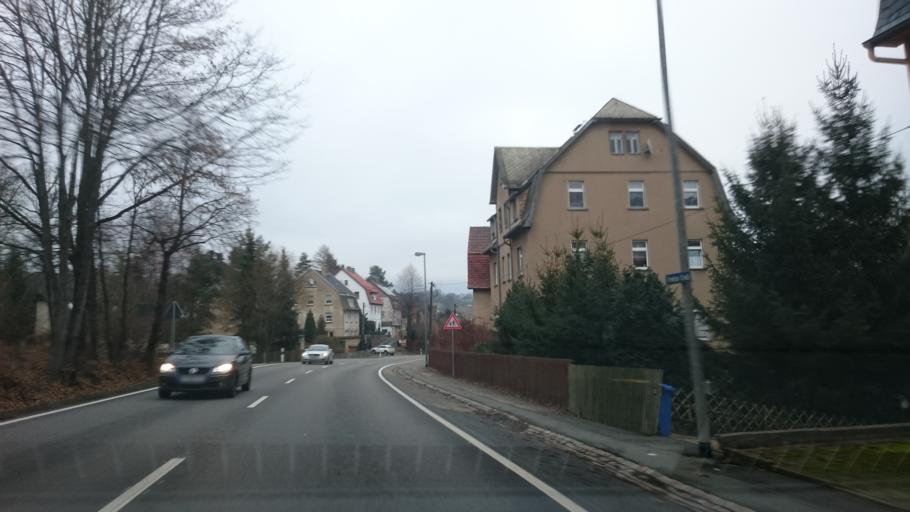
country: DE
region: Saxony
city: Mulsen
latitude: 50.7361
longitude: 12.5693
